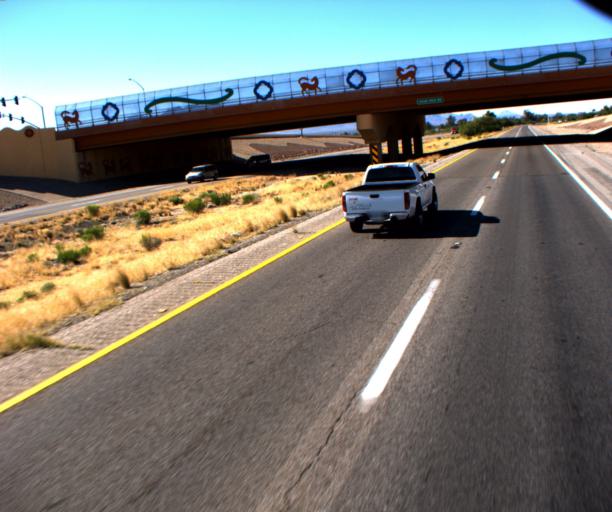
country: US
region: Arizona
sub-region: Pima County
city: Green Valley
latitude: 31.9067
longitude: -110.9858
